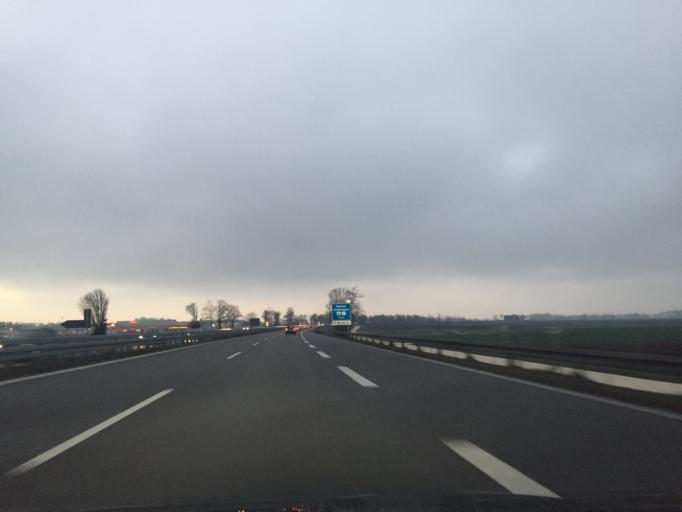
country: DE
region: Bavaria
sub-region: Upper Bavaria
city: Landsberg am Lech
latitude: 48.0571
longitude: 10.9025
